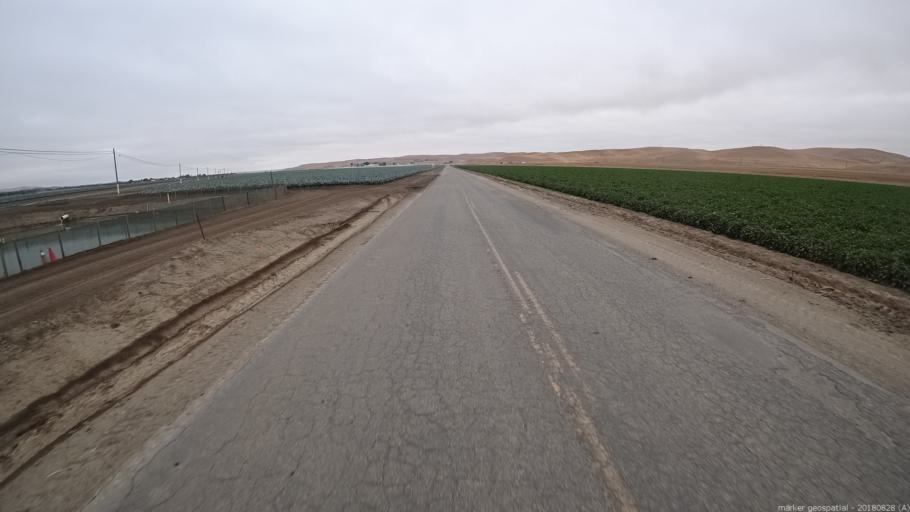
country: US
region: California
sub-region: San Luis Obispo County
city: Lake Nacimiento
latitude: 35.9992
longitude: -120.8862
